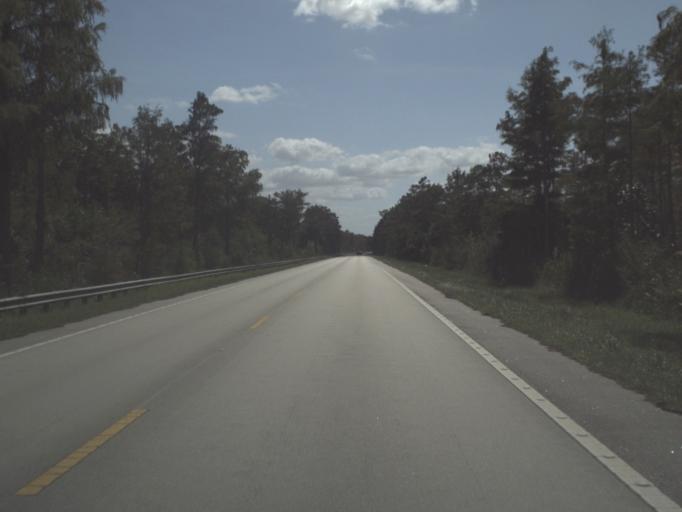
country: US
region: Florida
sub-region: Miami-Dade County
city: Kendall West
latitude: 25.8085
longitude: -80.8768
